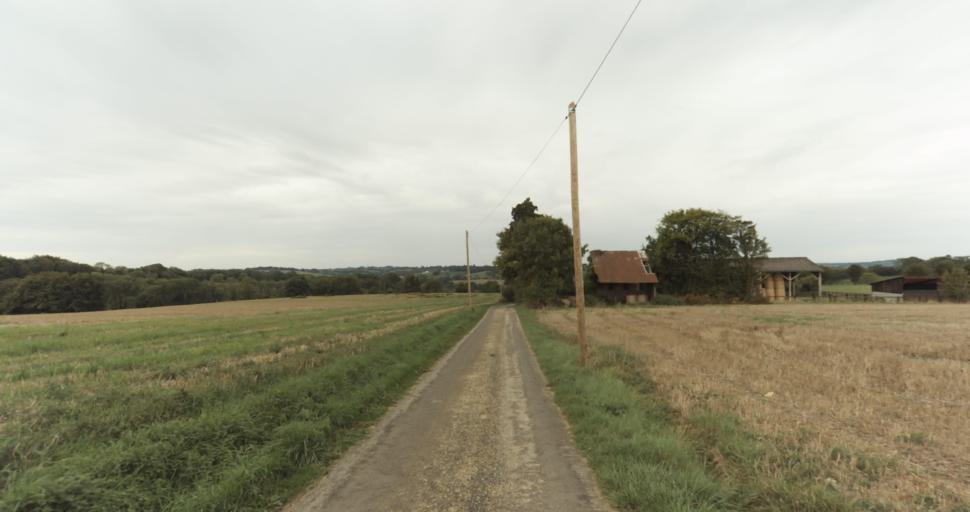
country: FR
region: Lower Normandy
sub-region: Departement de l'Orne
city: Sainte-Gauburge-Sainte-Colombe
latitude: 48.7435
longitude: 0.3654
